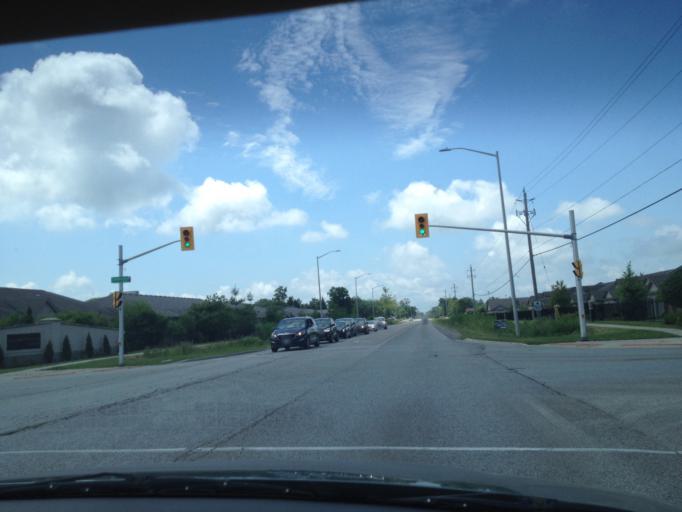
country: CA
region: Ontario
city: London
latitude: 43.0017
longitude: -81.3220
